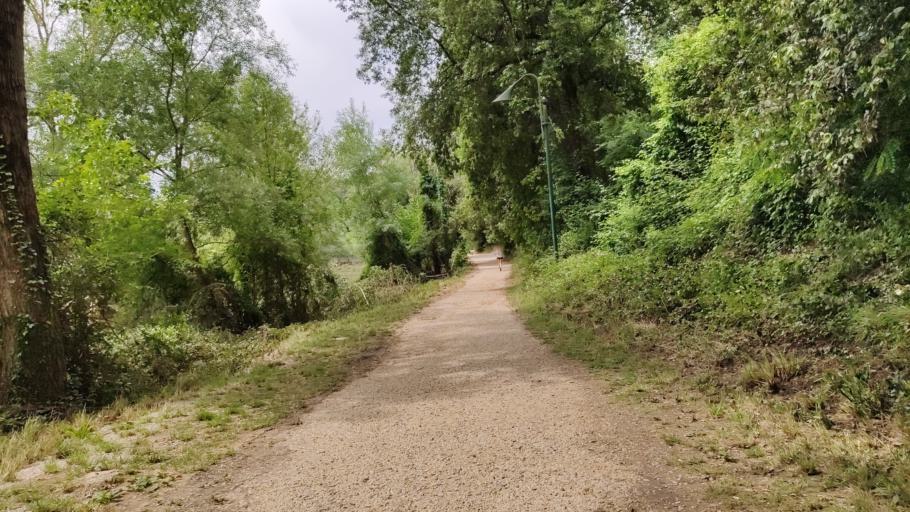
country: IT
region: Umbria
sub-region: Provincia di Terni
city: Amelia
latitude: 42.5620
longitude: 12.4198
